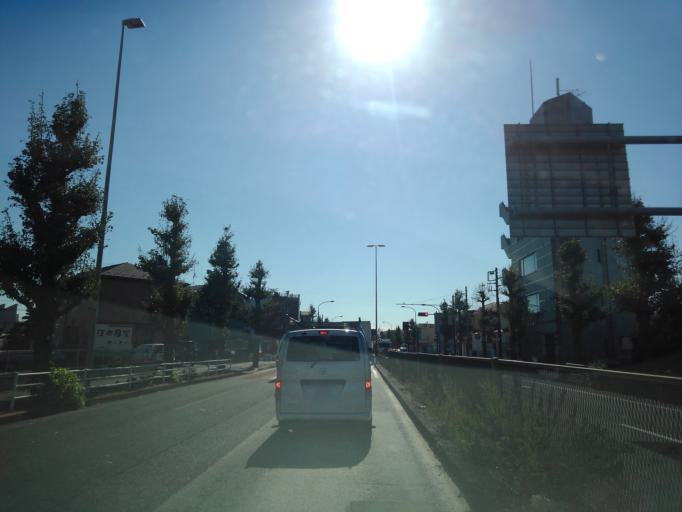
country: JP
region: Tokyo
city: Fussa
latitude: 35.7120
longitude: 139.3400
